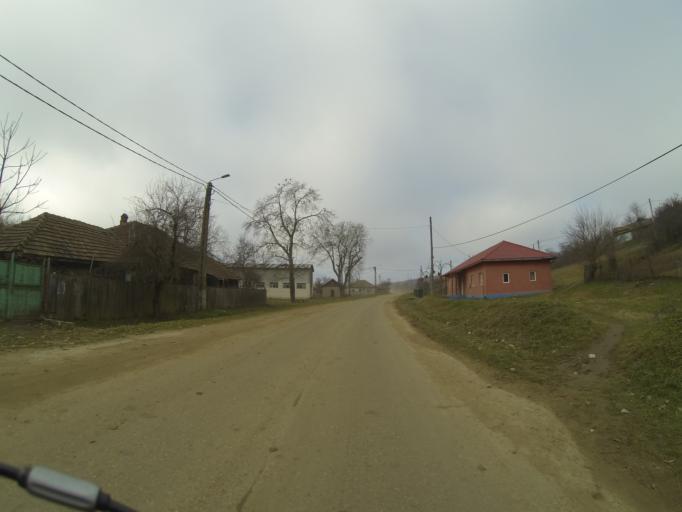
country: RO
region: Mehedinti
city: Padina Mica
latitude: 44.4916
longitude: 23.0020
